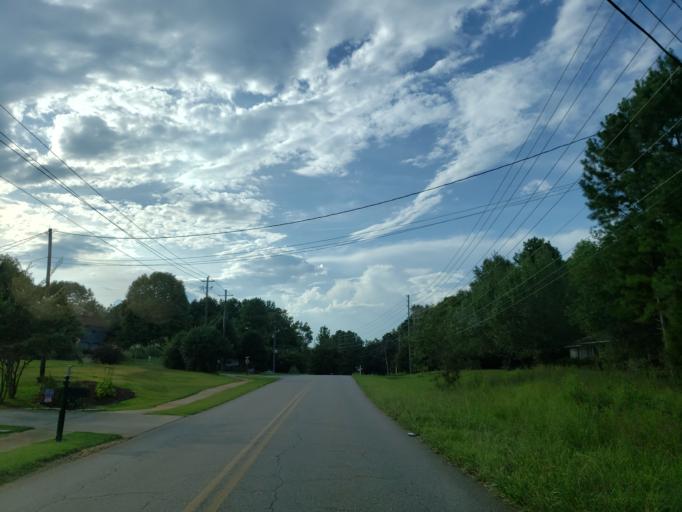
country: US
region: Georgia
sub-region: Bartow County
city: Euharlee
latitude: 34.1414
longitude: -84.9285
